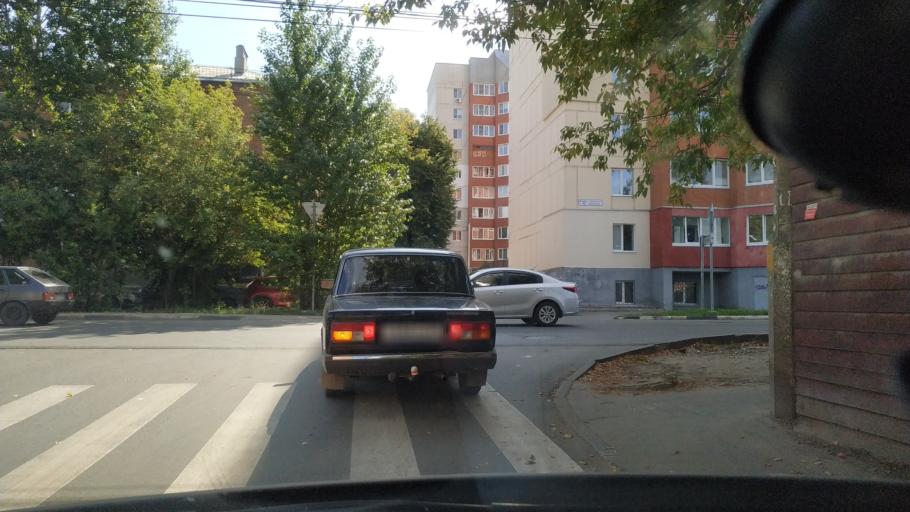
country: RU
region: Rjazan
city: Ryazan'
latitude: 54.6150
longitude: 39.7108
